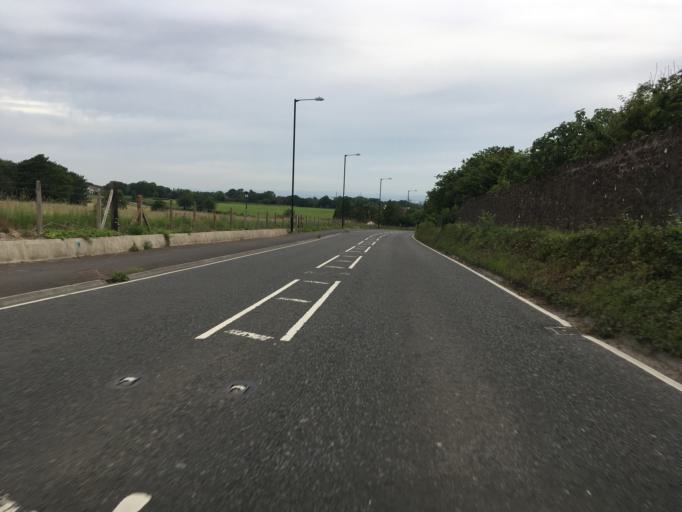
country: GB
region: England
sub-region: North Somerset
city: Easton-in-Gordano
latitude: 51.4642
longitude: -2.6681
